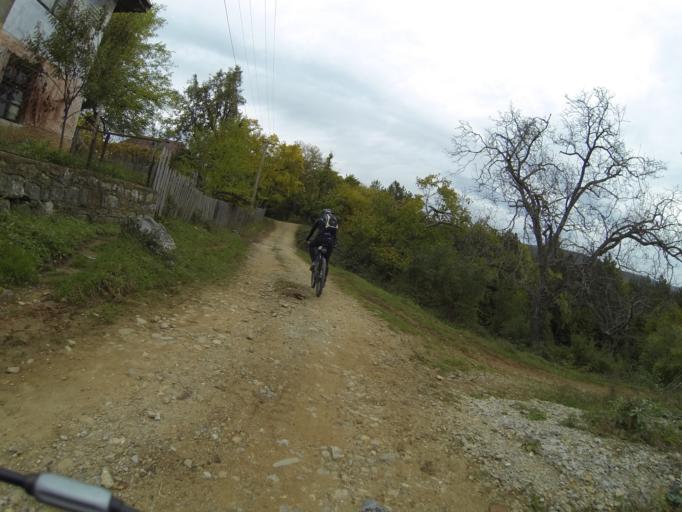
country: RO
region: Gorj
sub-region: Comuna Tismana
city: Sohodol
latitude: 45.0554
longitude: 22.8957
